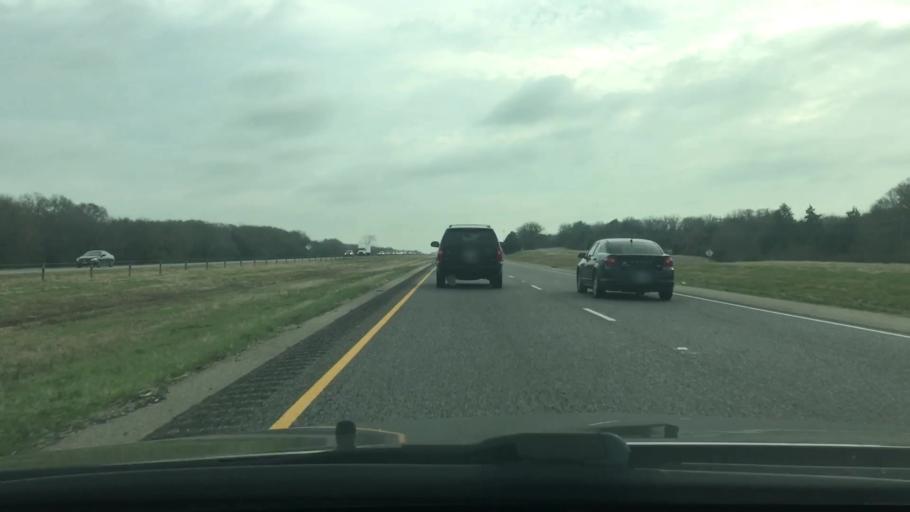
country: US
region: Texas
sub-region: Freestone County
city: Fairfield
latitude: 31.6253
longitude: -96.1577
